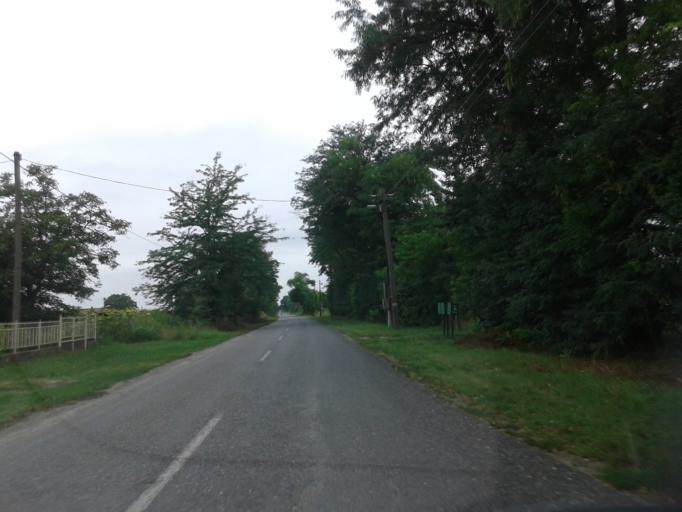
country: HU
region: Bacs-Kiskun
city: Tass
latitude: 47.0211
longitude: 19.0164
